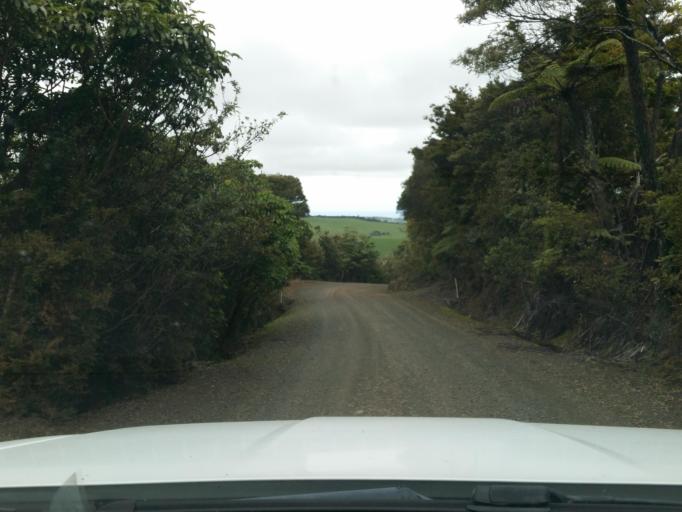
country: NZ
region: Northland
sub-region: Kaipara District
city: Dargaville
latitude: -35.7061
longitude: 173.6390
